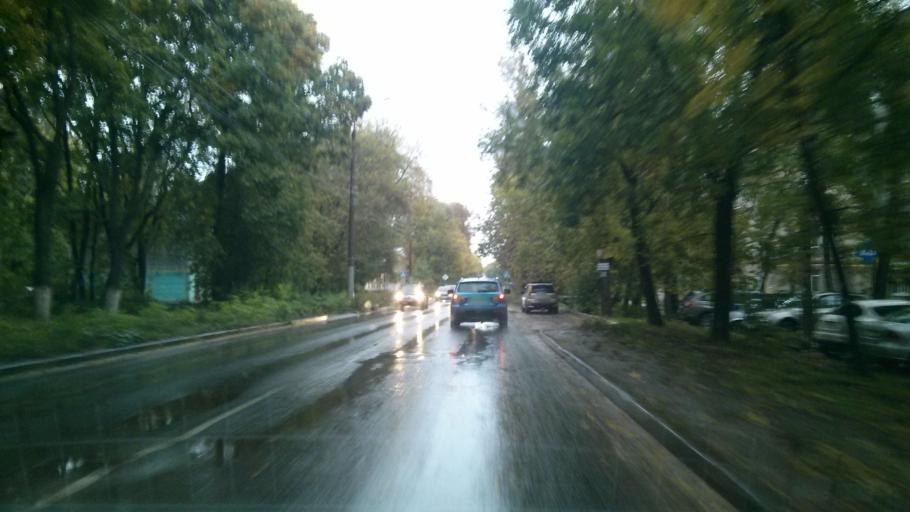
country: RU
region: Nizjnij Novgorod
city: Nizhniy Novgorod
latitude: 56.3099
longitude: 44.0077
